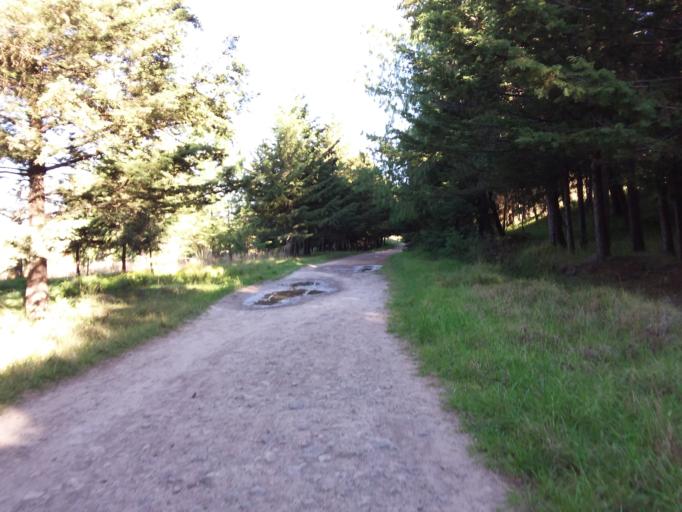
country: MX
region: Mexico
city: San Marcos Yachihuacaltepec
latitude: 19.3120
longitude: -99.6928
